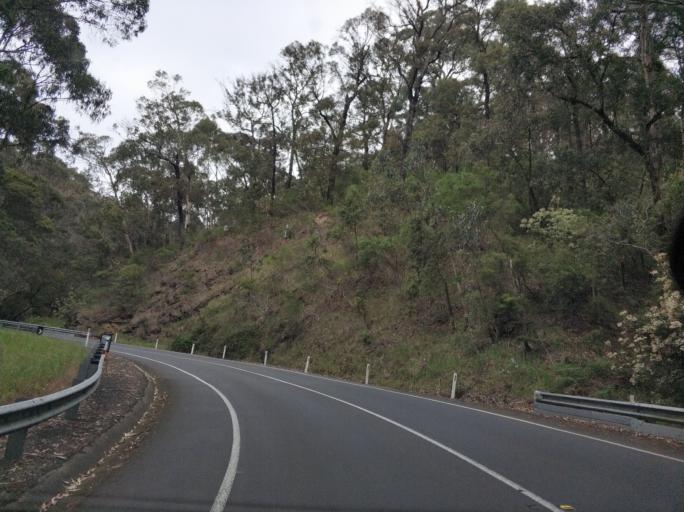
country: AU
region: Victoria
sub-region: Surf Coast
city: Anglesea
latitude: -38.4838
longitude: 144.0218
